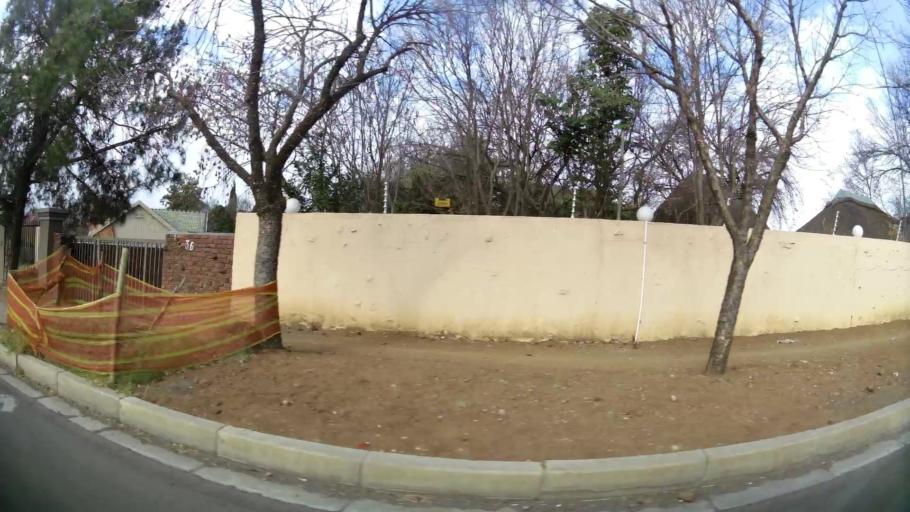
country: ZA
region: Orange Free State
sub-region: Mangaung Metropolitan Municipality
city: Bloemfontein
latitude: -29.0806
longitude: 26.2350
